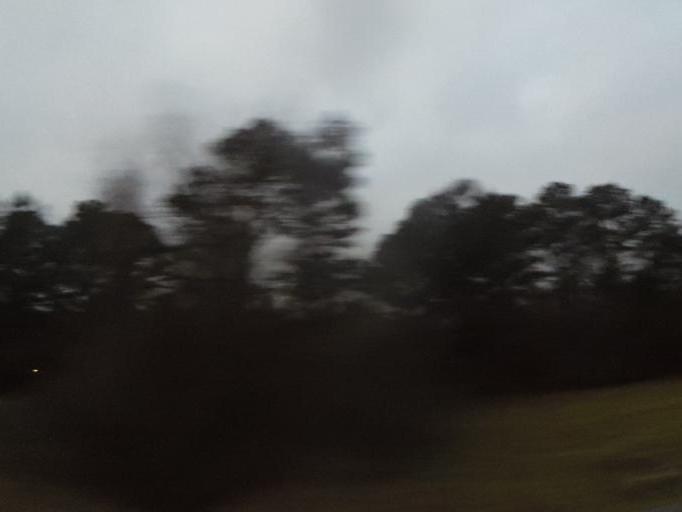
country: US
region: Alabama
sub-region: Cullman County
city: Cullman
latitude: 34.2467
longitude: -86.8868
